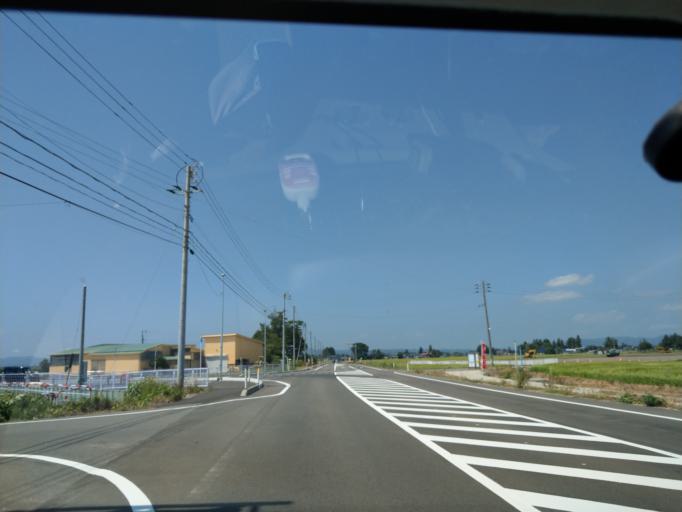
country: JP
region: Akita
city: Yokotemachi
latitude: 39.3279
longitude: 140.5162
